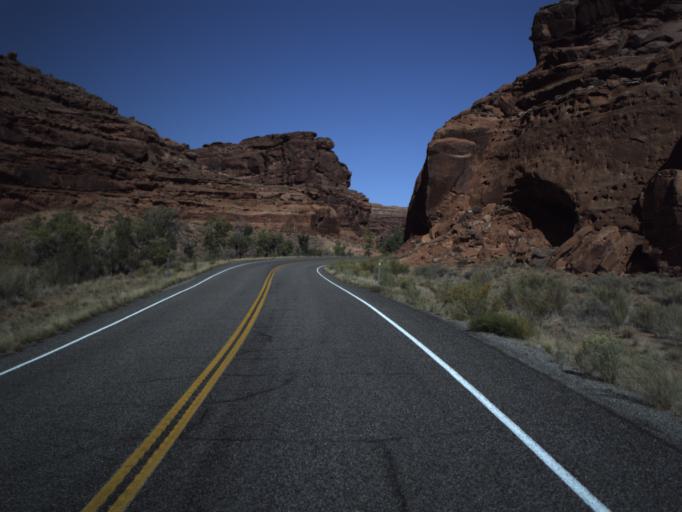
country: US
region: Utah
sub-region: San Juan County
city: Blanding
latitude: 37.9880
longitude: -110.4938
